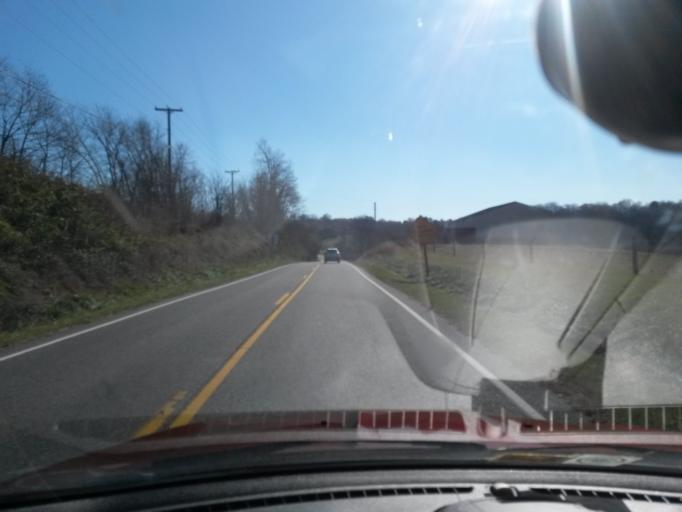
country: US
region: Virginia
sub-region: City of Bedford
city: Bedford
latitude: 37.3575
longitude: -79.5372
